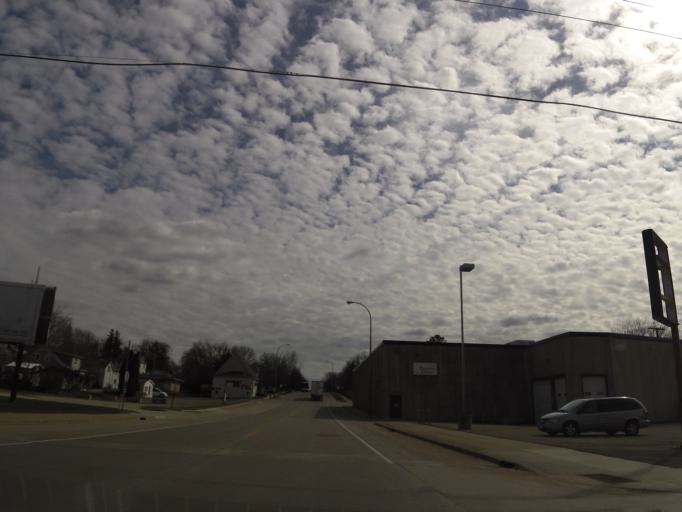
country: US
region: Minnesota
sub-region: Fillmore County
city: Spring Valley
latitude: 43.6869
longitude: -92.3892
